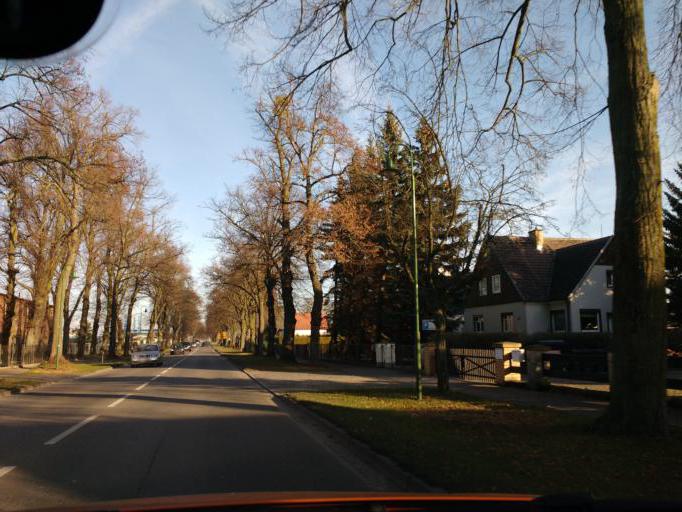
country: DE
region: Brandenburg
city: Werneuchen
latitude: 52.6343
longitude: 13.7429
